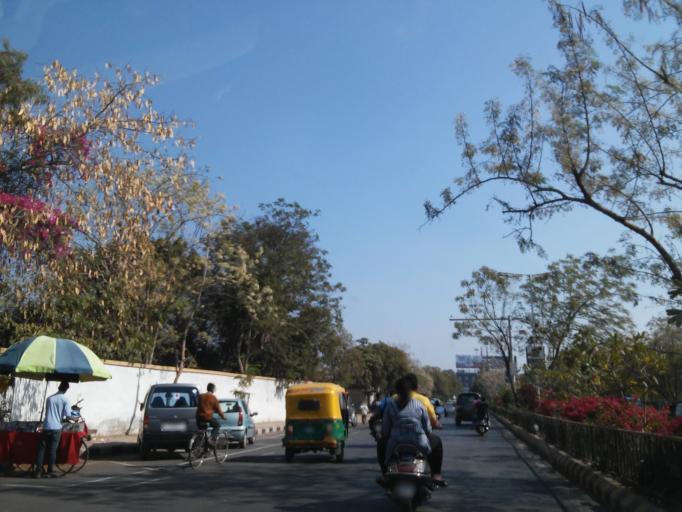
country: IN
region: Gujarat
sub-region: Ahmadabad
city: Sarkhej
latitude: 23.0299
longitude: 72.5283
